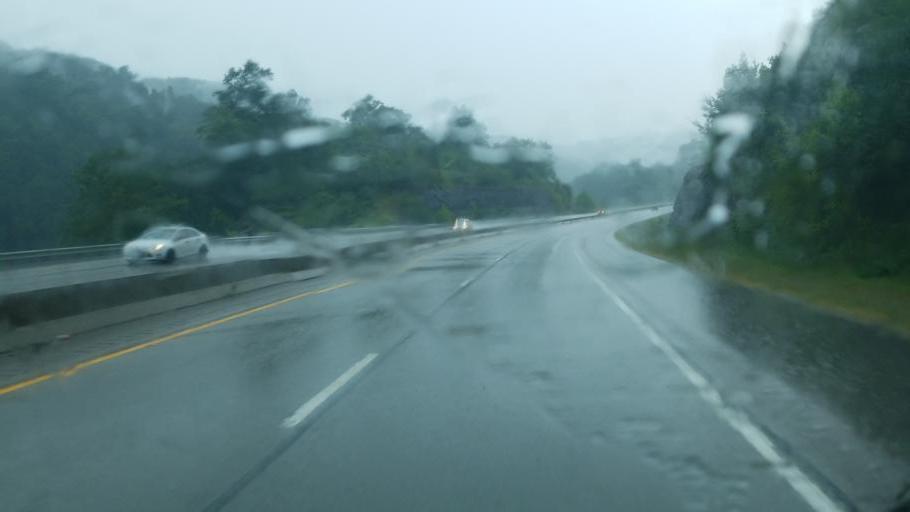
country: US
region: West Virginia
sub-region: Mingo County
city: Williamson
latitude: 37.6140
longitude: -82.3403
